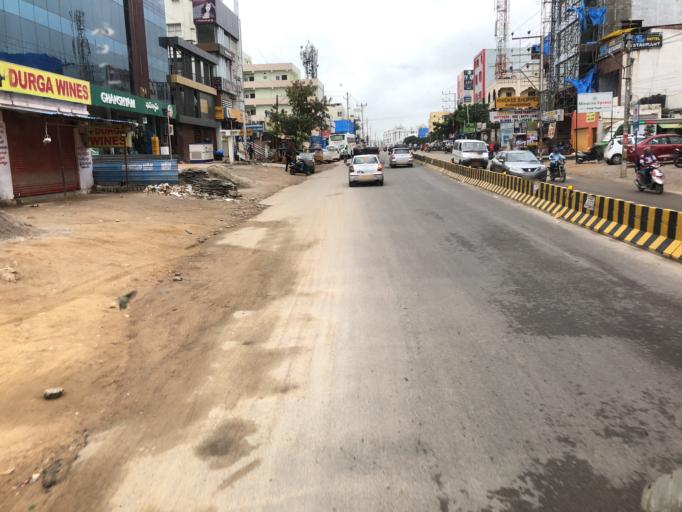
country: IN
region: Telangana
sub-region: Medak
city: Serilingampalle
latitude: 17.4598
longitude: 78.3555
